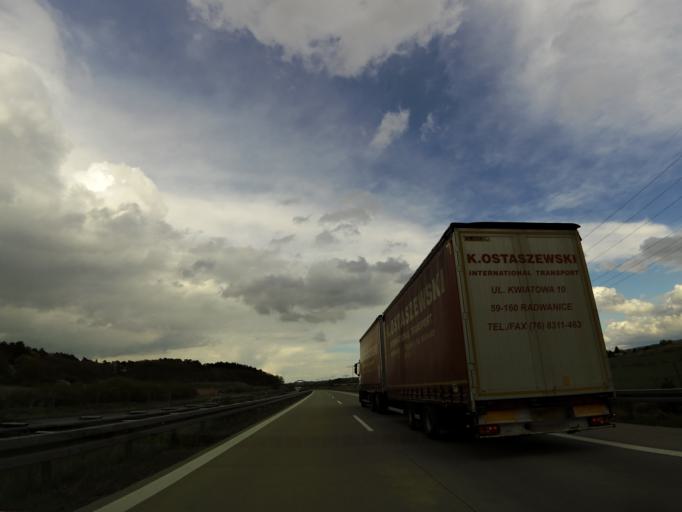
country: DE
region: Saxony-Anhalt
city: Blankenburg
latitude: 51.8056
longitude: 10.9663
